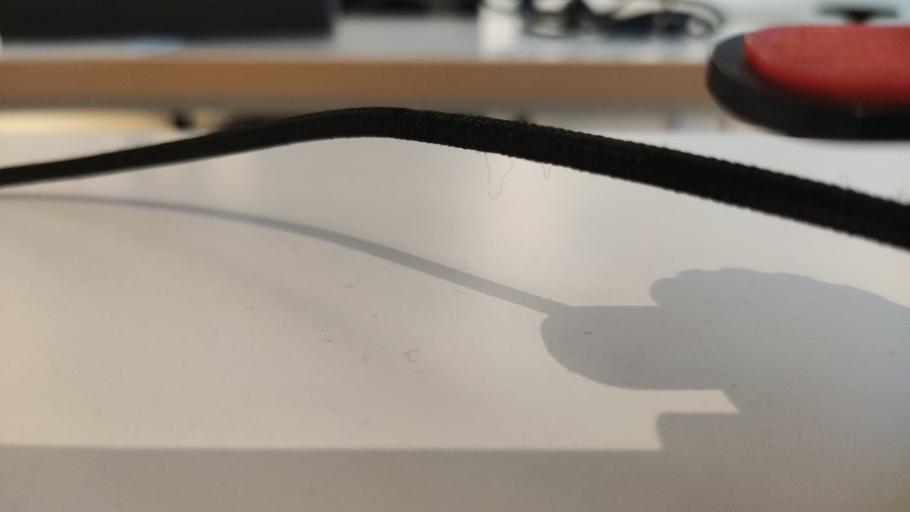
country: RU
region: Moskovskaya
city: Ruza
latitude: 55.8052
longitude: 36.2923
